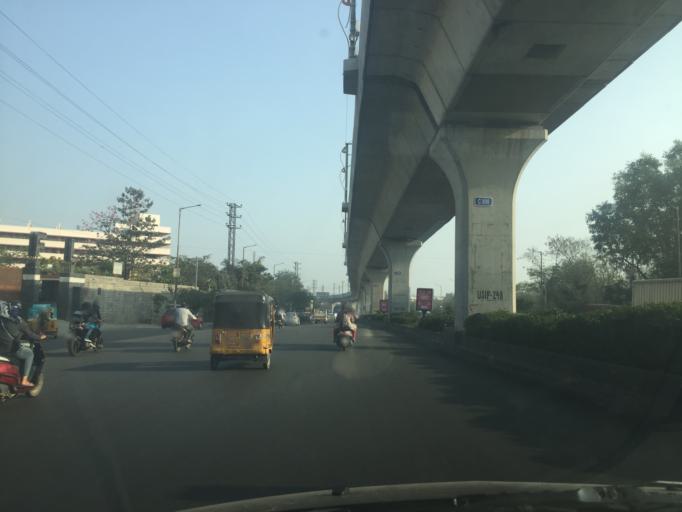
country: IN
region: Telangana
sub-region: Rangareddi
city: Uppal Kalan
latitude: 17.4051
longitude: 78.5563
